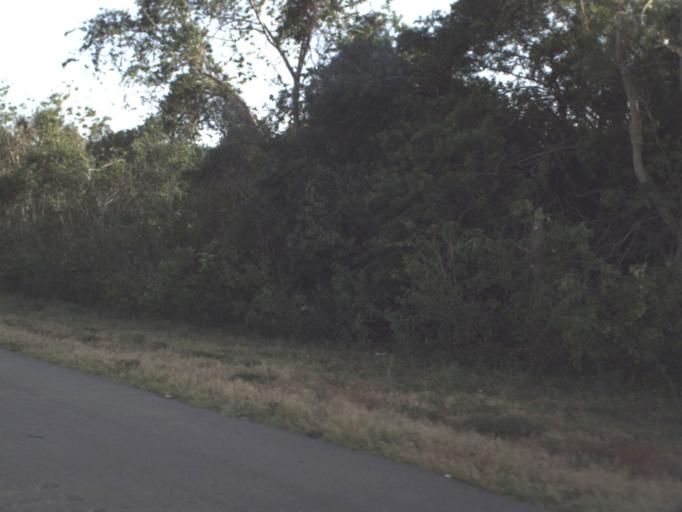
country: US
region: Florida
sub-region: Brevard County
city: Mims
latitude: 28.6282
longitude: -80.8543
